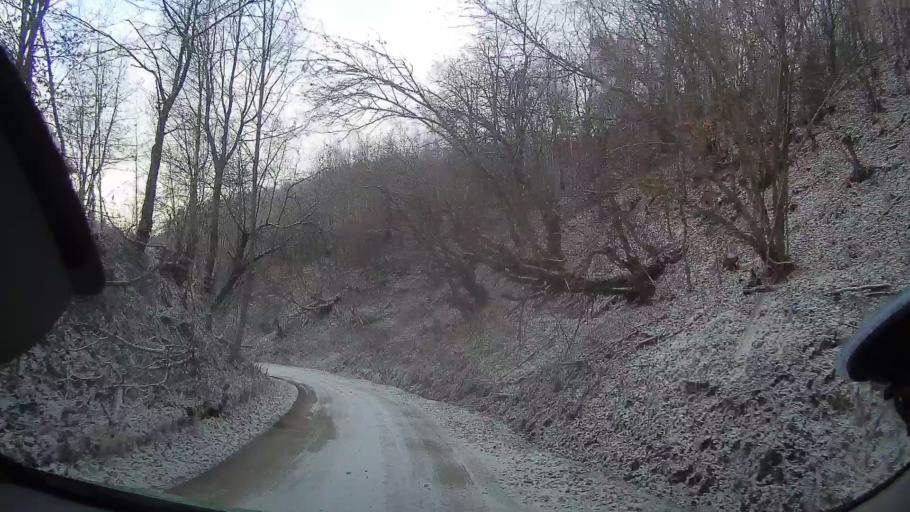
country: RO
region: Cluj
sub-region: Comuna Valea Ierii
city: Valea Ierii
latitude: 46.6687
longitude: 23.3328
